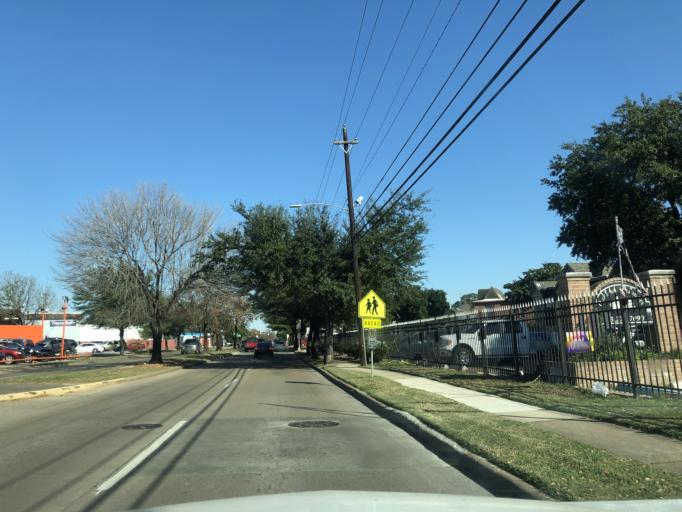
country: US
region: Texas
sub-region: Harris County
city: Bellaire
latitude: 29.6884
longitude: -95.5054
